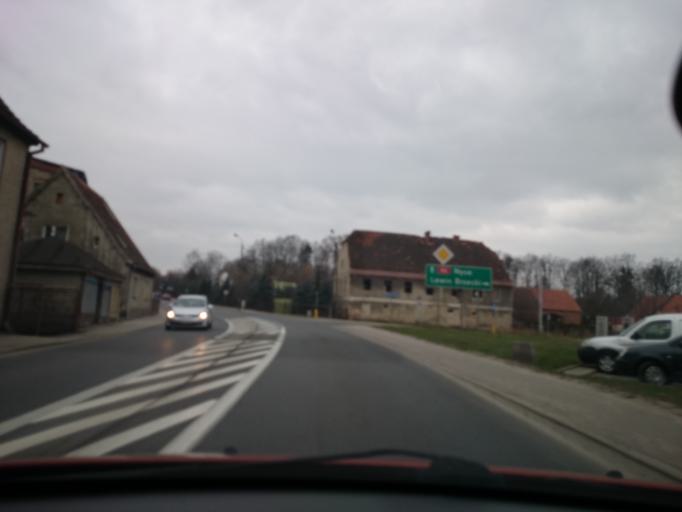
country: PL
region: Opole Voivodeship
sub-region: Powiat opolski
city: Niemodlin
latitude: 50.6426
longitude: 17.6116
